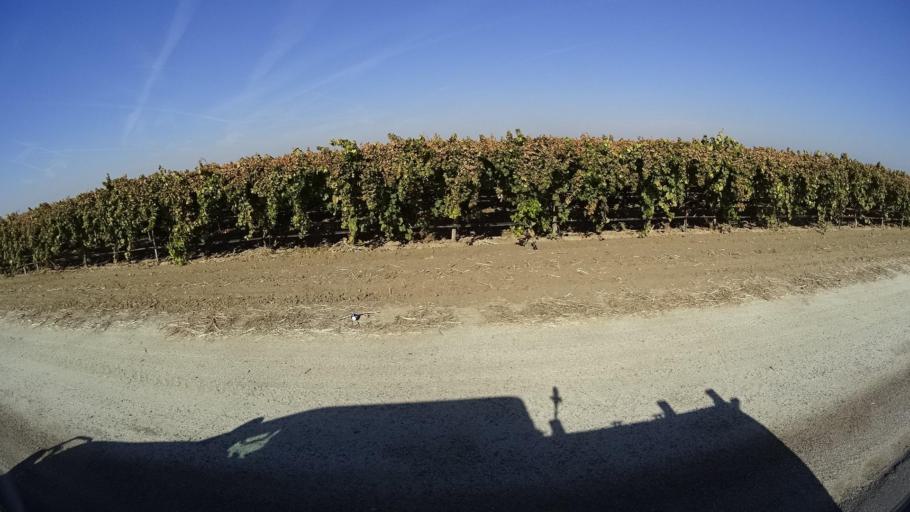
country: US
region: California
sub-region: Kern County
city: McFarland
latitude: 35.6456
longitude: -119.2120
